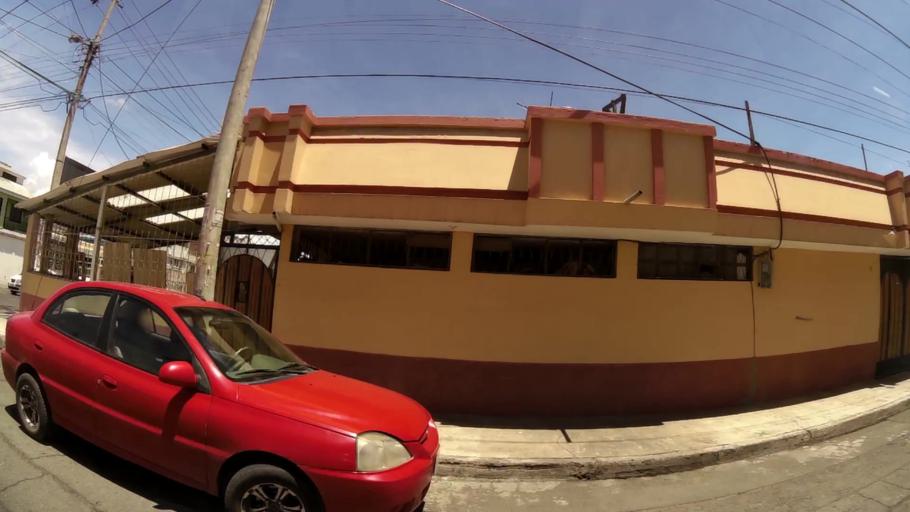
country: EC
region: Chimborazo
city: Riobamba
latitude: -1.6812
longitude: -78.6537
